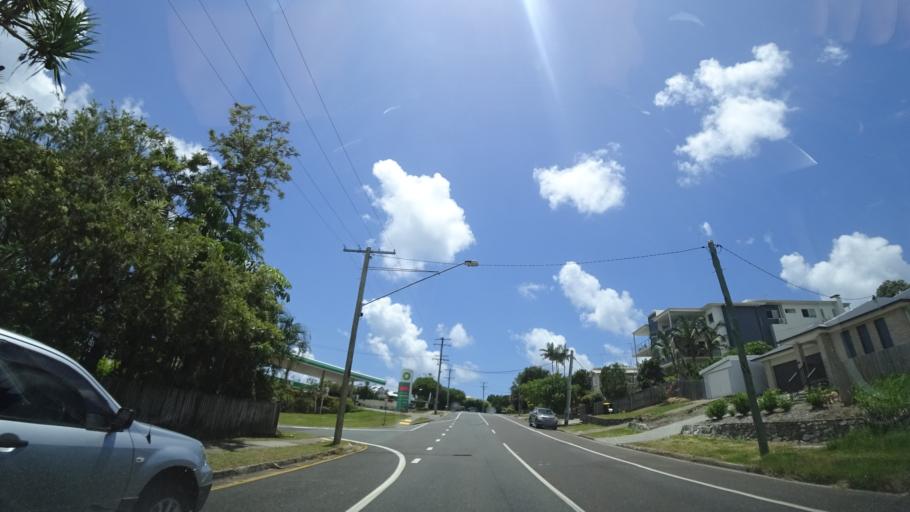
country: AU
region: Queensland
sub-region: Sunshine Coast
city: Coolum Beach
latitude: -26.5338
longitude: 153.0876
